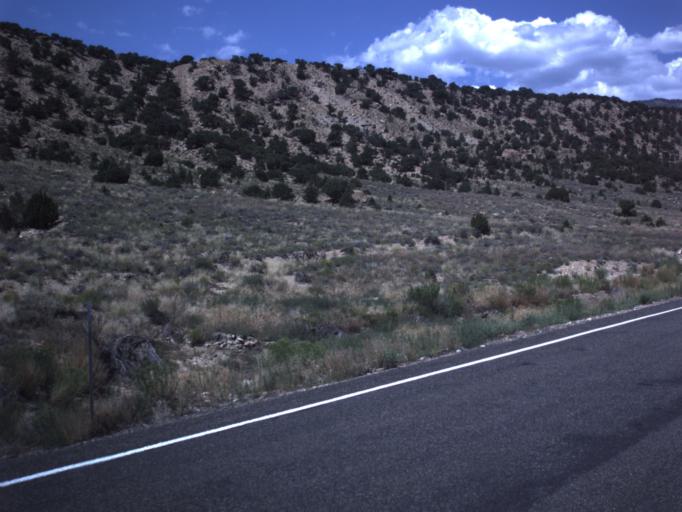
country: US
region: Utah
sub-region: Emery County
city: Orangeville
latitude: 39.2639
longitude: -111.1001
